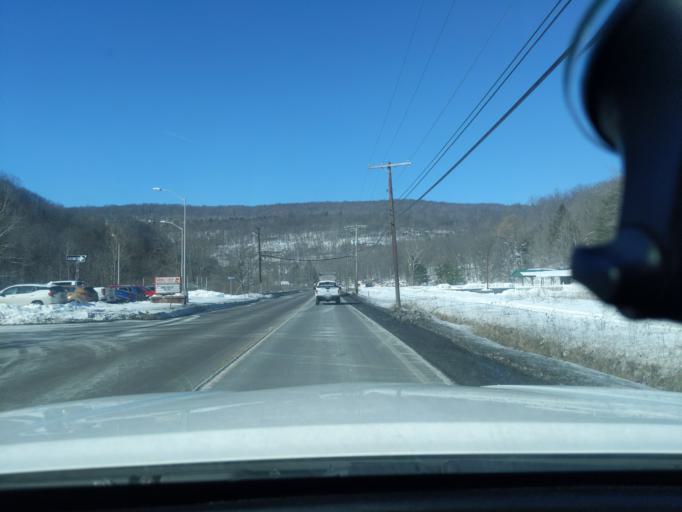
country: US
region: Maryland
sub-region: Allegany County
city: Lonaconing
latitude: 39.5788
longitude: -78.9636
